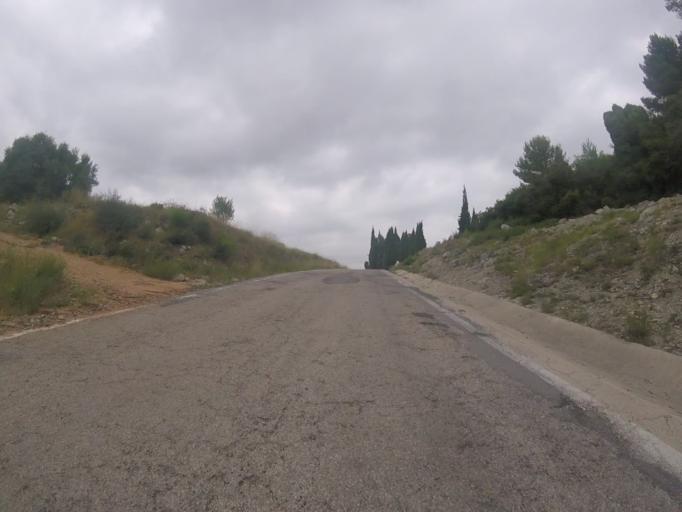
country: ES
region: Valencia
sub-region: Provincia de Castello
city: Cabanes
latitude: 40.1222
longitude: 0.0452
